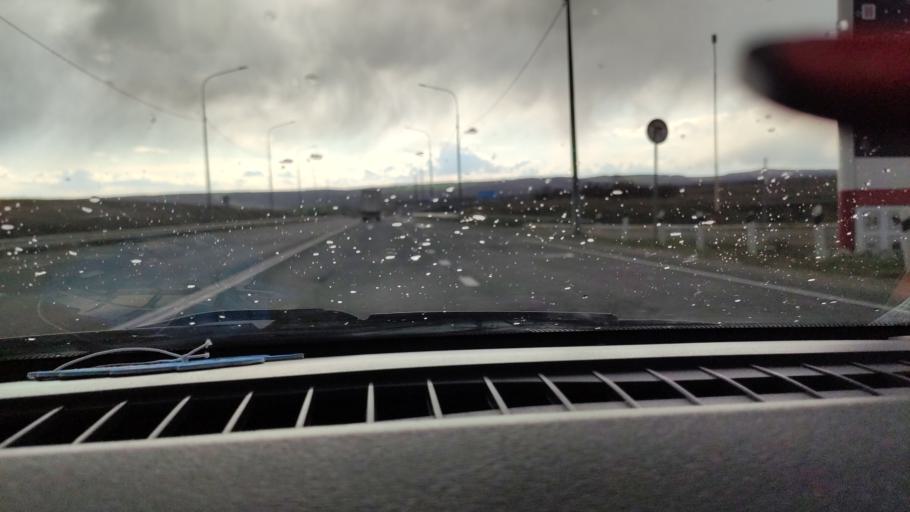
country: RU
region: Saratov
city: Yelshanka
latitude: 51.8305
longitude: 46.4228
